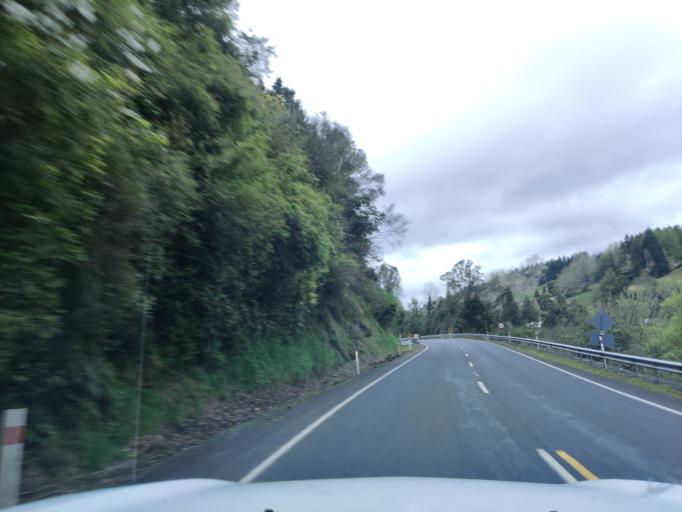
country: NZ
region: Waikato
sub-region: Otorohanga District
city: Otorohanga
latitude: -38.6087
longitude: 175.2168
